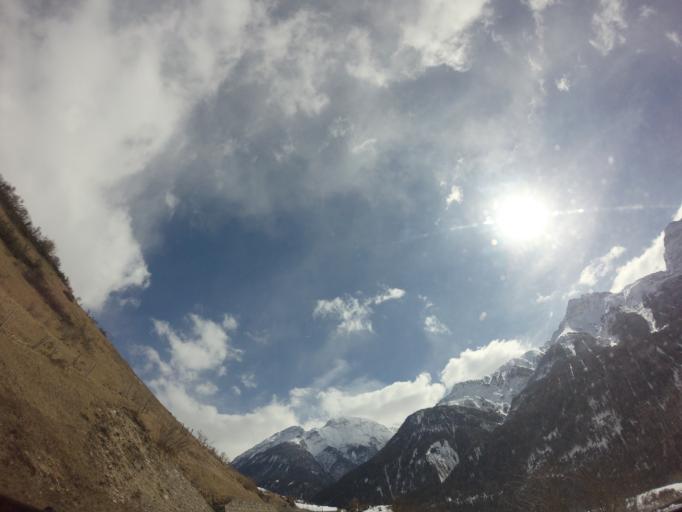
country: CH
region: Grisons
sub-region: Inn District
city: Scuol
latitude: 46.8109
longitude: 10.3308
